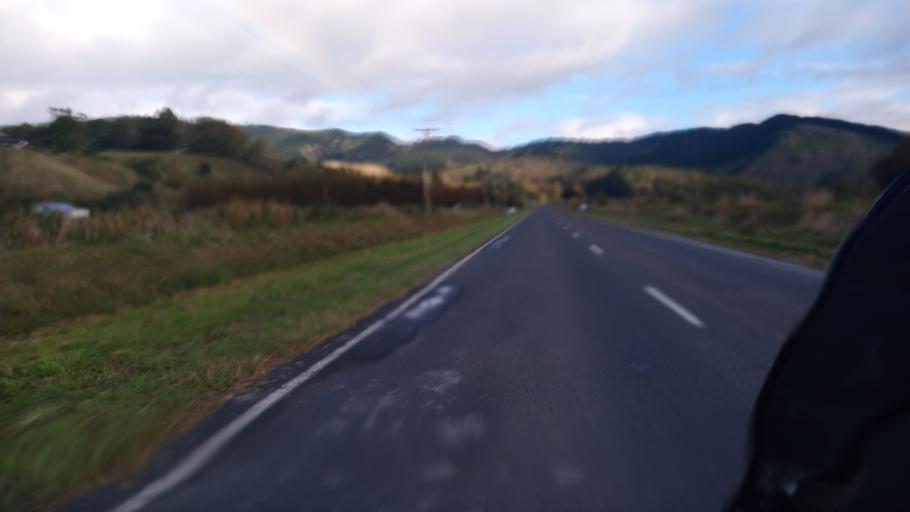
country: NZ
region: Gisborne
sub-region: Gisborne District
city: Gisborne
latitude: -38.6340
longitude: 177.8354
